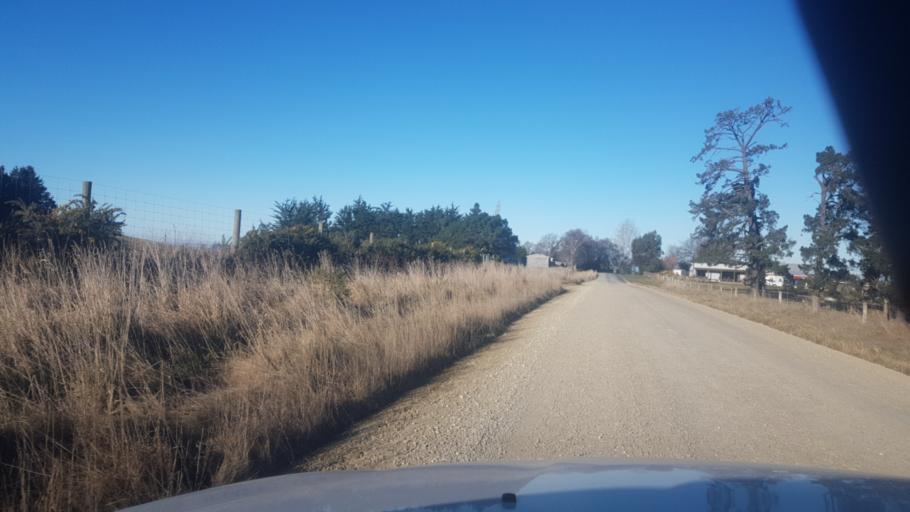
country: NZ
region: Canterbury
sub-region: Timaru District
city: Pleasant Point
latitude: -44.3717
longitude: 171.0758
